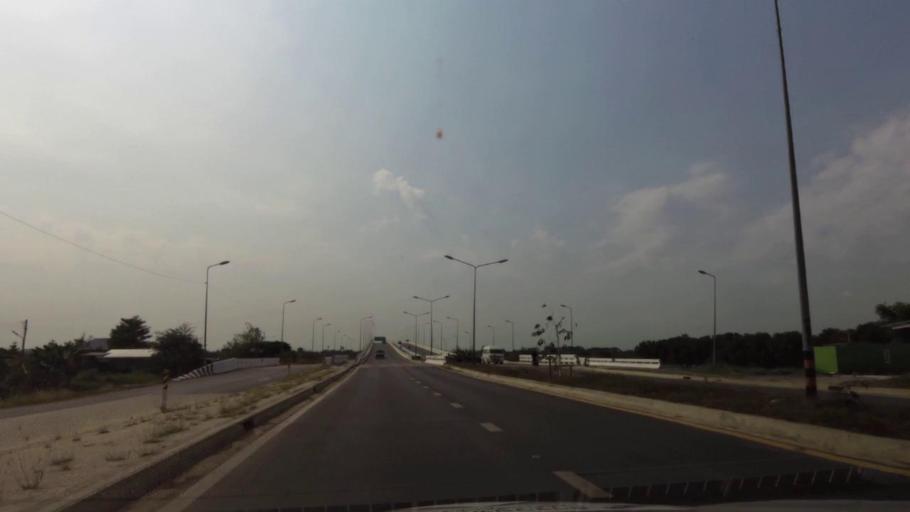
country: TH
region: Phra Nakhon Si Ayutthaya
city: Phra Nakhon Si Ayutthaya
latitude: 14.3313
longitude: 100.5871
